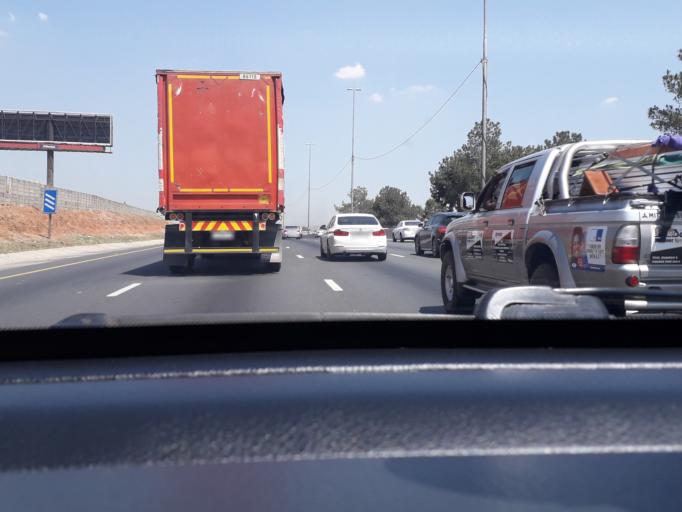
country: ZA
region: Gauteng
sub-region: City of Johannesburg Metropolitan Municipality
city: Modderfontein
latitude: -26.0954
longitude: 28.1182
